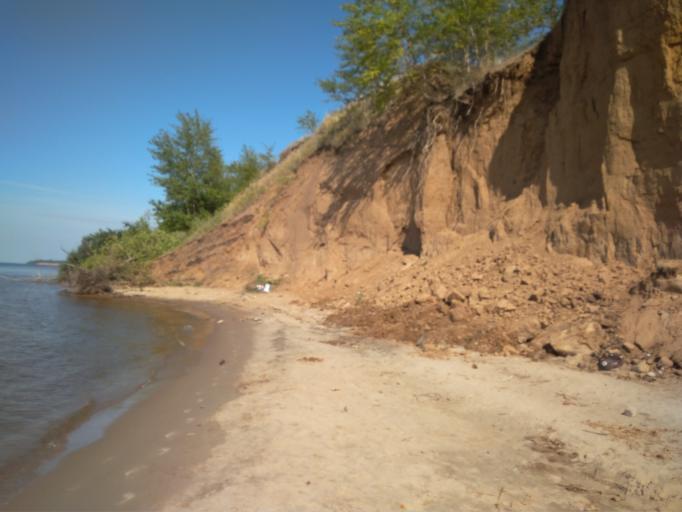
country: RU
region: Ulyanovsk
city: Staraya Mayna
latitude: 54.6131
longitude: 48.9029
